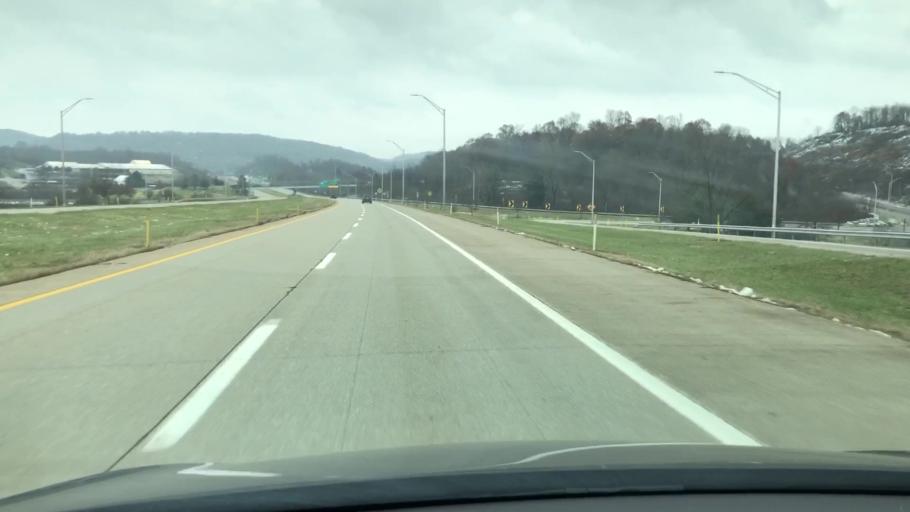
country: US
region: Pennsylvania
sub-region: Westmoreland County
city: New Stanton
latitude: 40.2370
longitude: -79.6045
